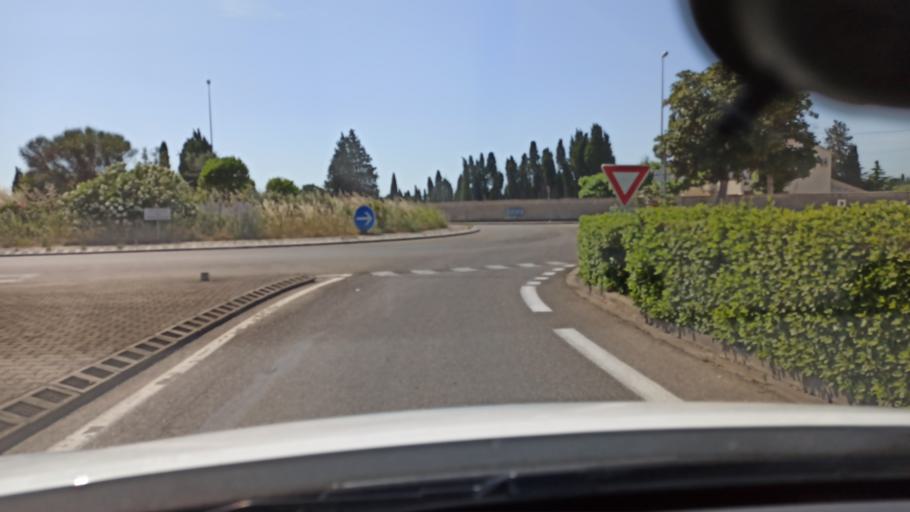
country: FR
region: Provence-Alpes-Cote d'Azur
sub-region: Departement des Bouches-du-Rhone
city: Chateaurenard
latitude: 43.8711
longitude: 4.8511
